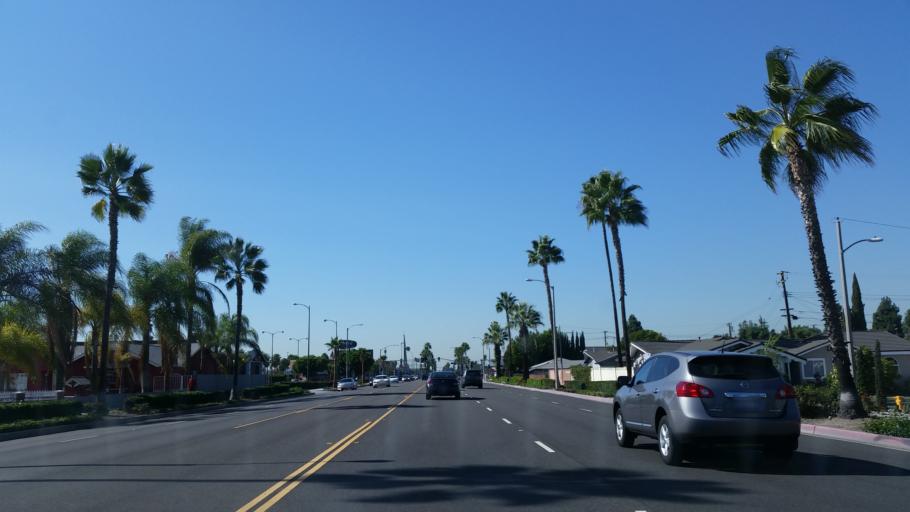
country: US
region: California
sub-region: Orange County
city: Buena Park
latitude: 33.8468
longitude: -117.9823
